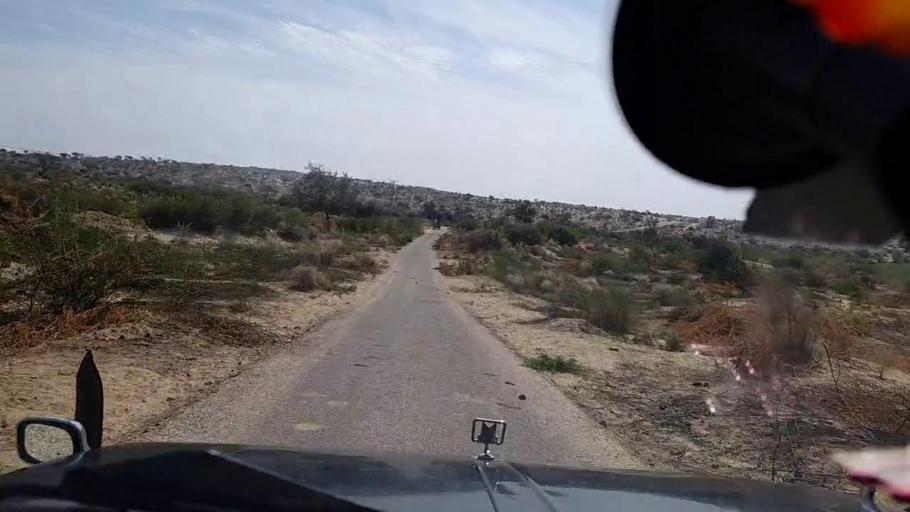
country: PK
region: Sindh
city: Diplo
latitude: 24.4057
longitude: 69.5857
